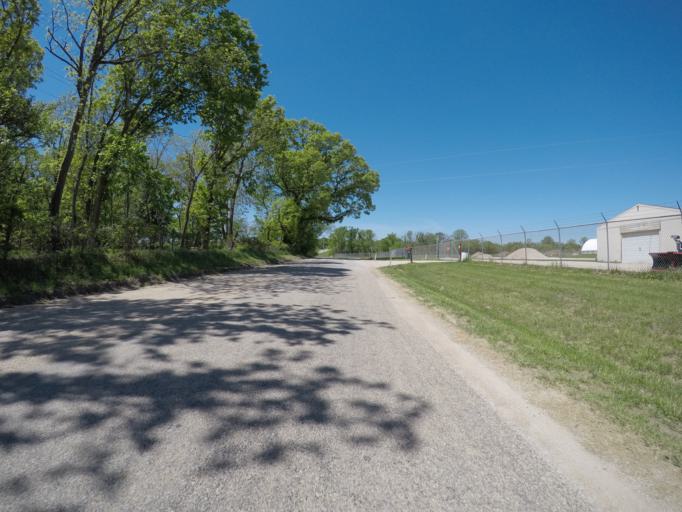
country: US
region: Kansas
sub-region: Shawnee County
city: Topeka
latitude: 39.0231
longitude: -95.5473
